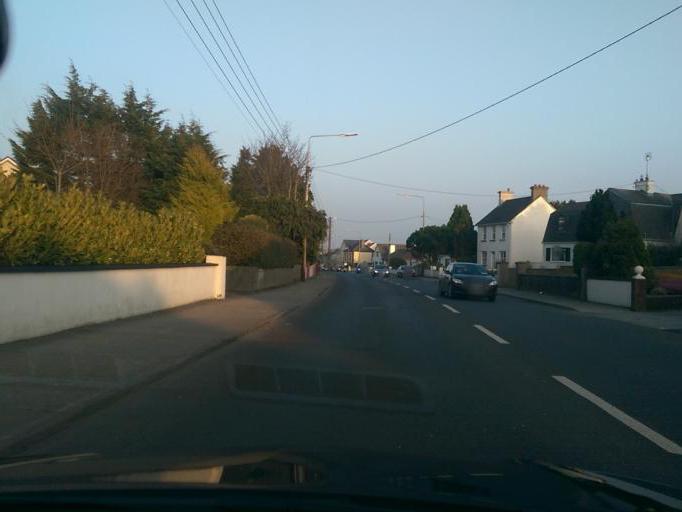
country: IE
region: Connaught
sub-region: County Galway
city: Loughrea
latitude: 53.2005
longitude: -8.5793
